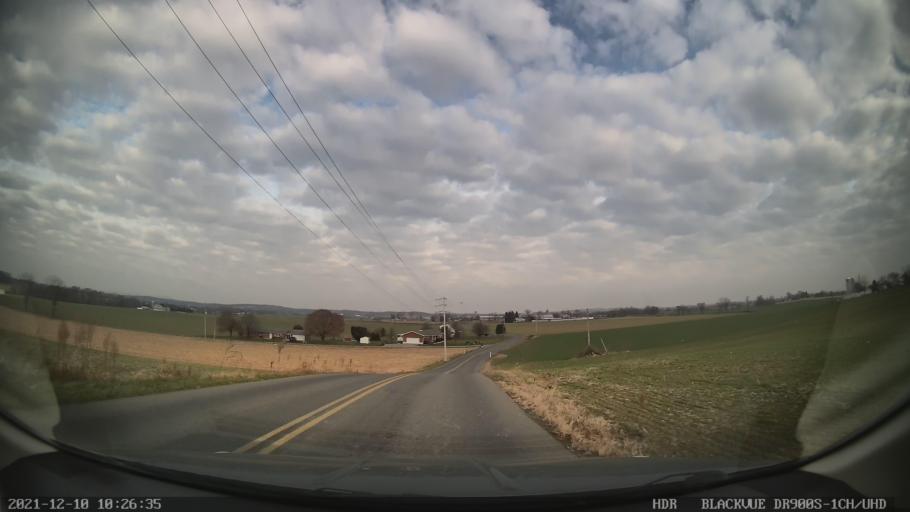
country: US
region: Pennsylvania
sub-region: Berks County
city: Kutztown
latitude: 40.4981
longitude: -75.7434
